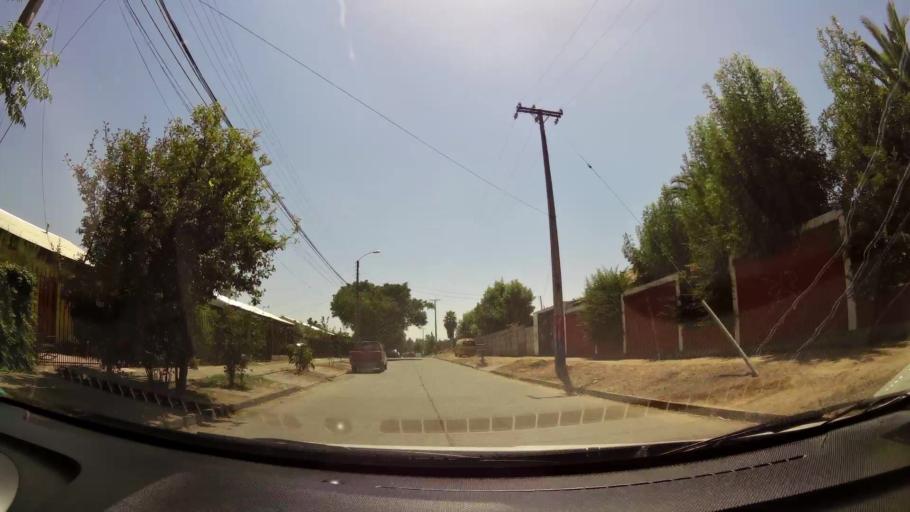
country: CL
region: Maule
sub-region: Provincia de Talca
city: Talca
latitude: -35.4268
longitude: -71.6279
